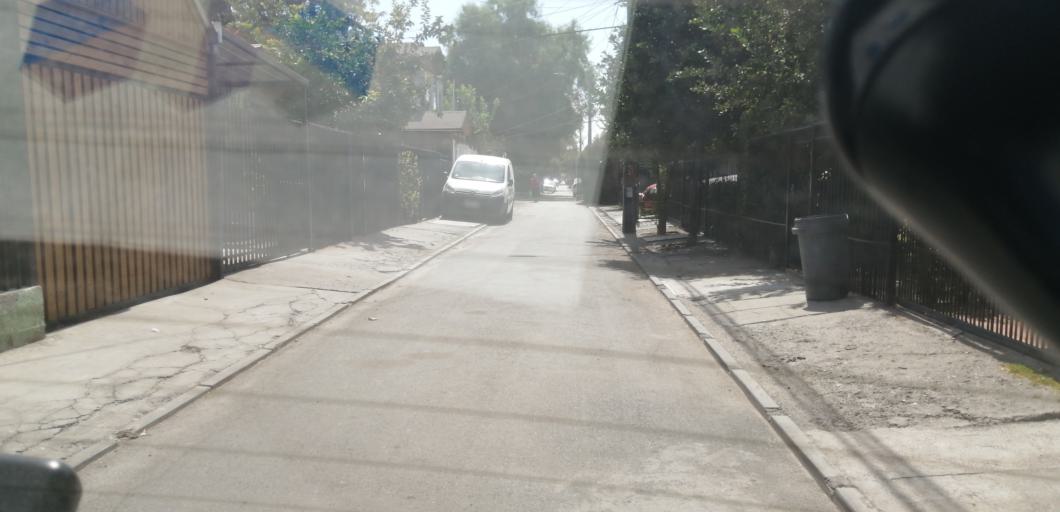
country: CL
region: Santiago Metropolitan
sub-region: Provincia de Santiago
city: Lo Prado
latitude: -33.4656
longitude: -70.7436
